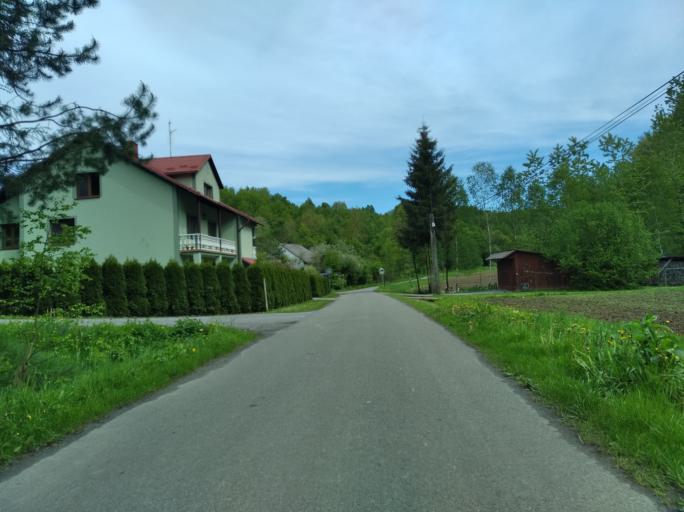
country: PL
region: Subcarpathian Voivodeship
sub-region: Powiat strzyzowski
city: Strzyzow
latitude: 49.9251
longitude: 21.7537
